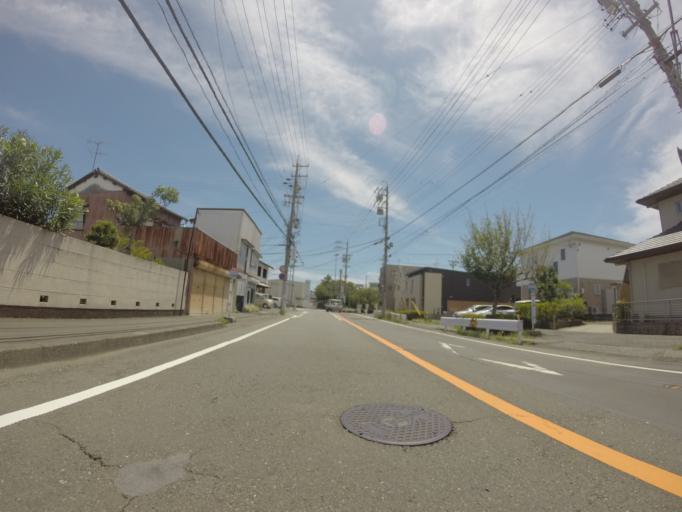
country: JP
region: Shizuoka
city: Shizuoka-shi
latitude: 35.0001
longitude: 138.4712
